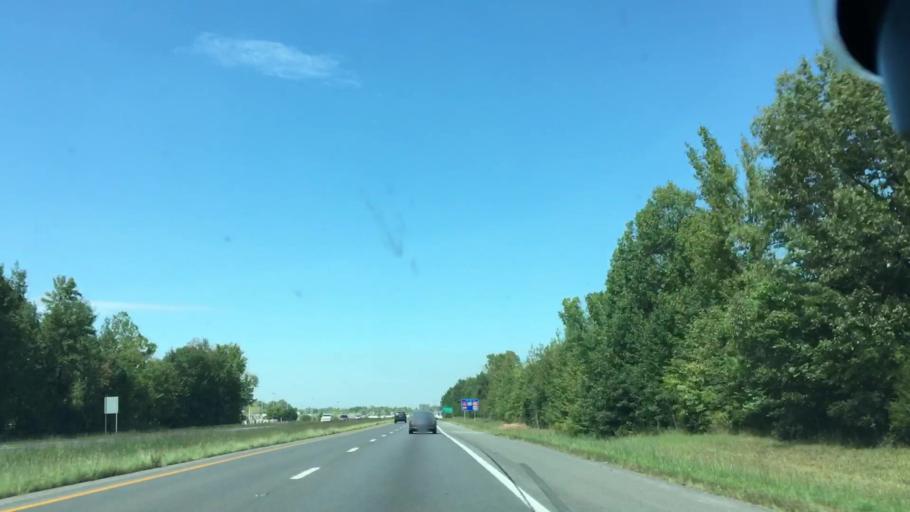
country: US
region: Kentucky
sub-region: Hopkins County
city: Madisonville
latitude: 37.3141
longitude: -87.4705
